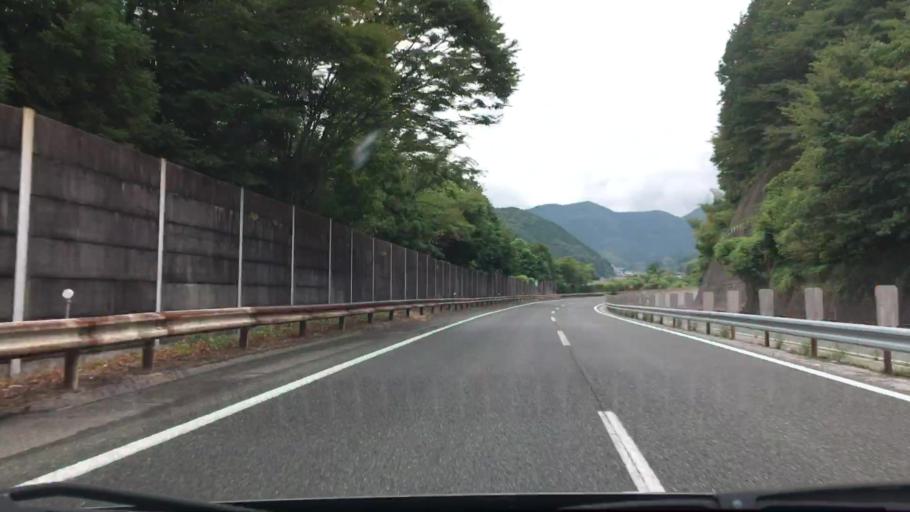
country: JP
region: Okayama
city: Niimi
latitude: 34.9704
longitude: 133.3595
